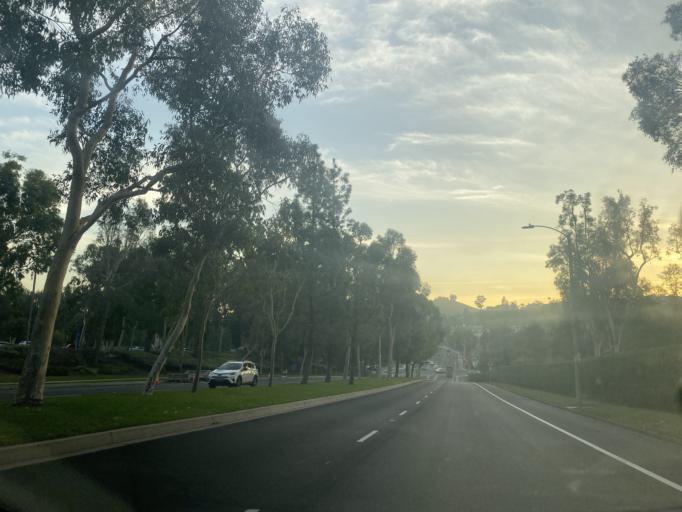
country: US
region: California
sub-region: Orange County
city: North Tustin
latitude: 33.7969
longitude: -117.7701
